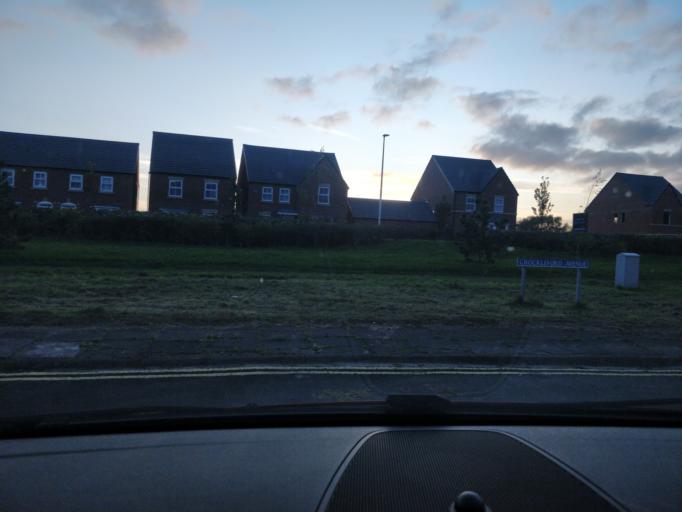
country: GB
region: England
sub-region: Sefton
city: Southport
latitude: 53.6302
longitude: -2.9836
